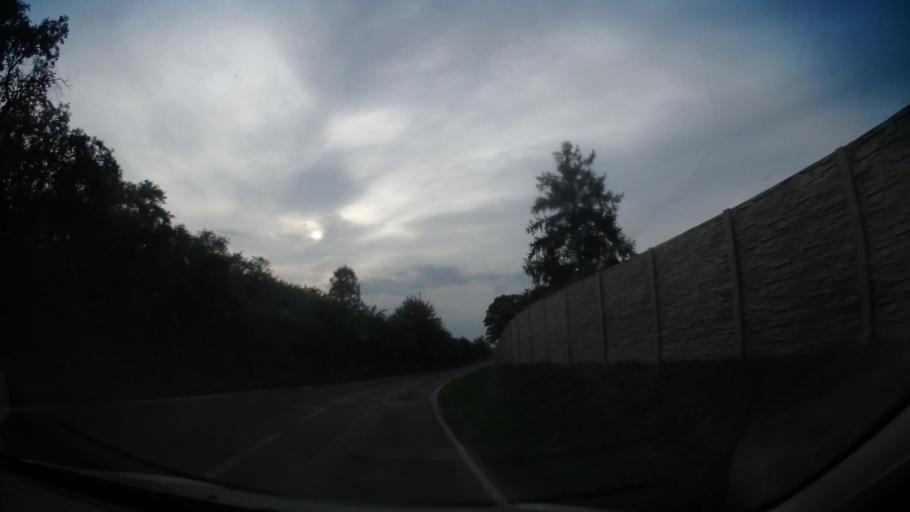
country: CZ
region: Central Bohemia
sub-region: Okres Kutna Hora
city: Caslav
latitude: 49.9019
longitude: 15.4166
